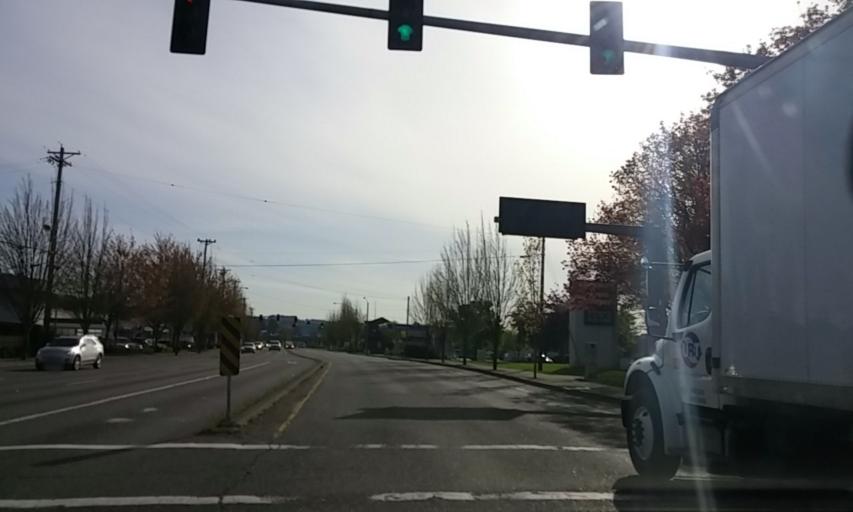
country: US
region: Oregon
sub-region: Washington County
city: Beaverton
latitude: 45.4894
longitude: -122.7975
